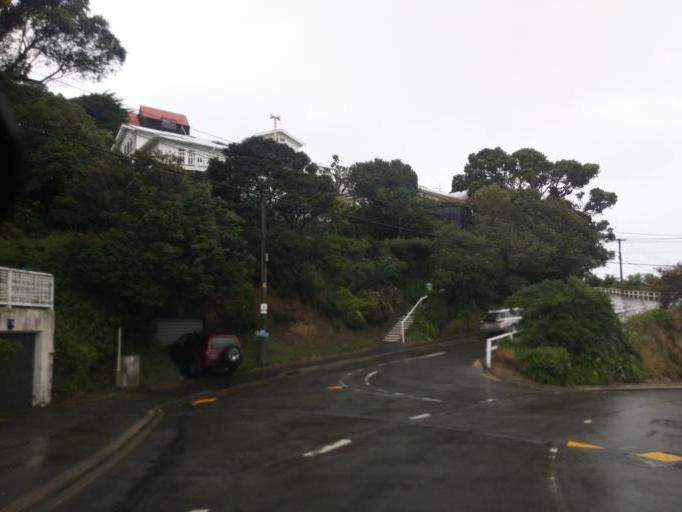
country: NZ
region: Wellington
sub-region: Wellington City
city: Wellington
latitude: -41.2618
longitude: 174.7798
